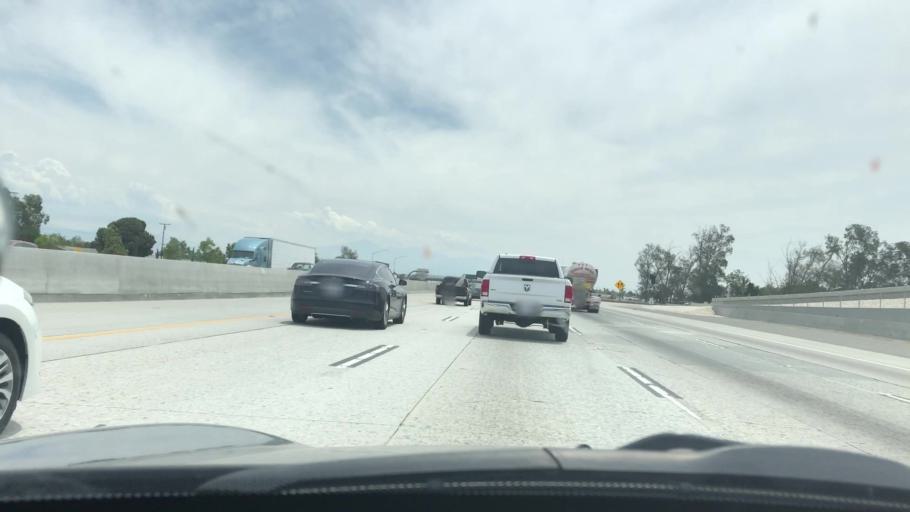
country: US
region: California
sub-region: San Bernardino County
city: Fontana
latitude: 34.0668
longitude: -117.4523
